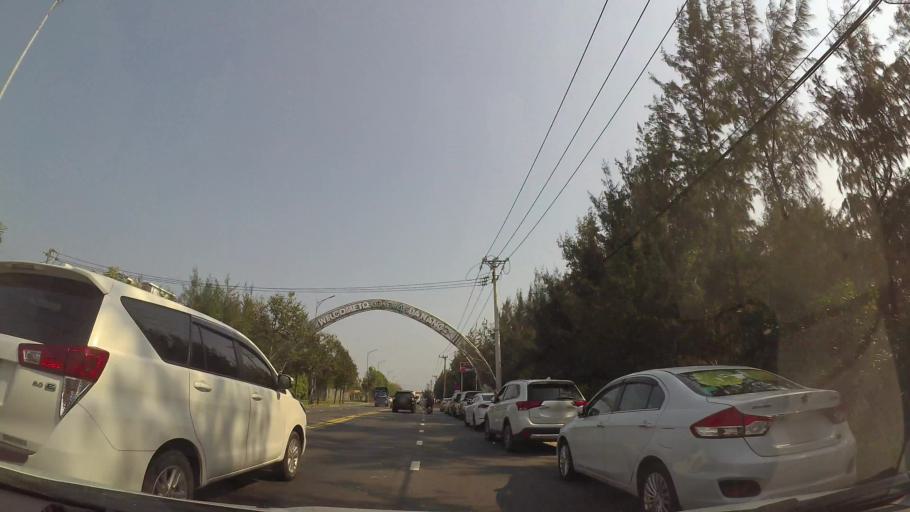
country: VN
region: Da Nang
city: Ngu Hanh Son
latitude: 15.9695
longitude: 108.2830
